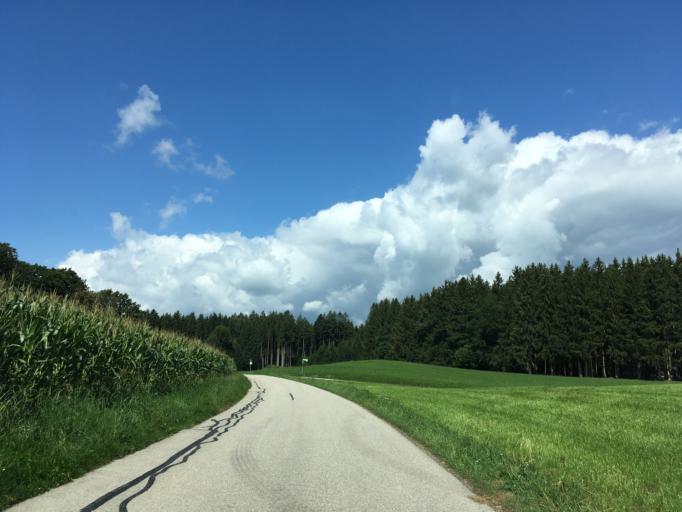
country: DE
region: Bavaria
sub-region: Upper Bavaria
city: Pittenhart
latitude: 47.9726
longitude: 12.3698
